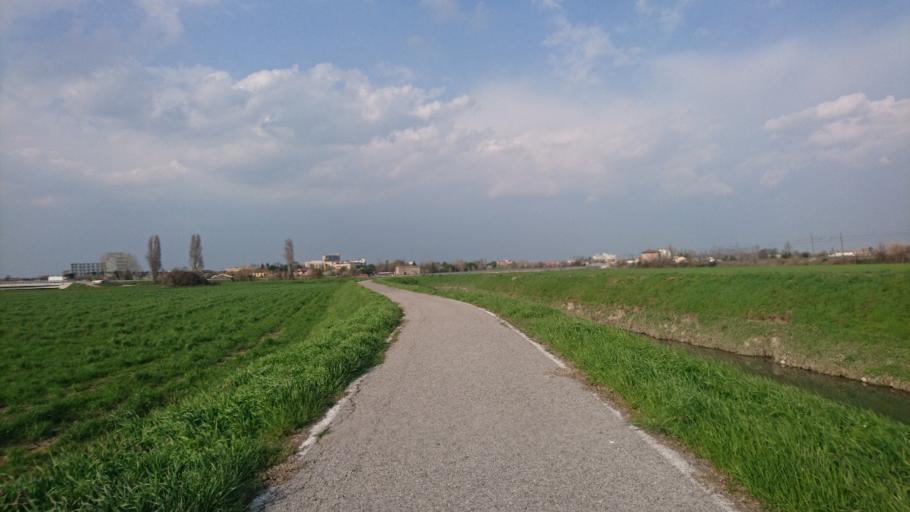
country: IT
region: Veneto
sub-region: Provincia di Padova
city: Montegrotto Terme
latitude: 45.3169
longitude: 11.7892
